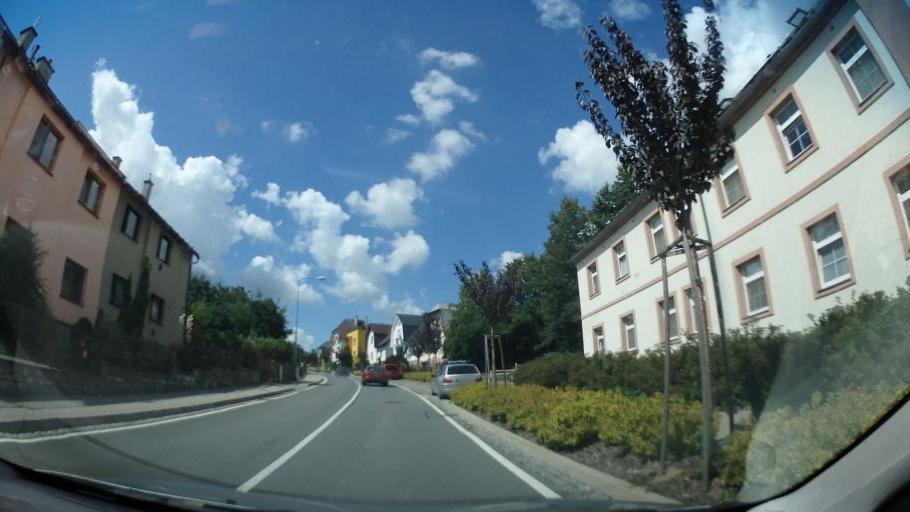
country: CZ
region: Olomoucky
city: Zabreh
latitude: 49.8822
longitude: 16.8629
